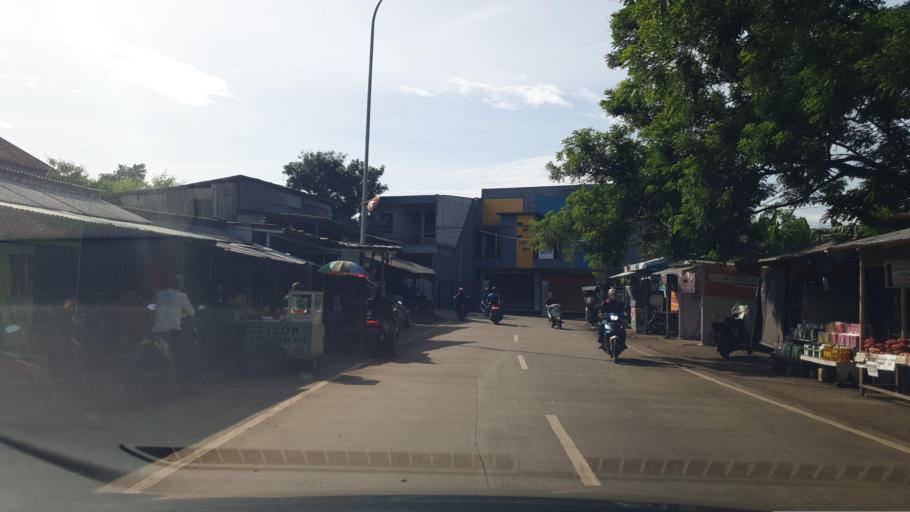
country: ID
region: West Java
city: Sawangan
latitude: -6.3775
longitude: 106.7880
